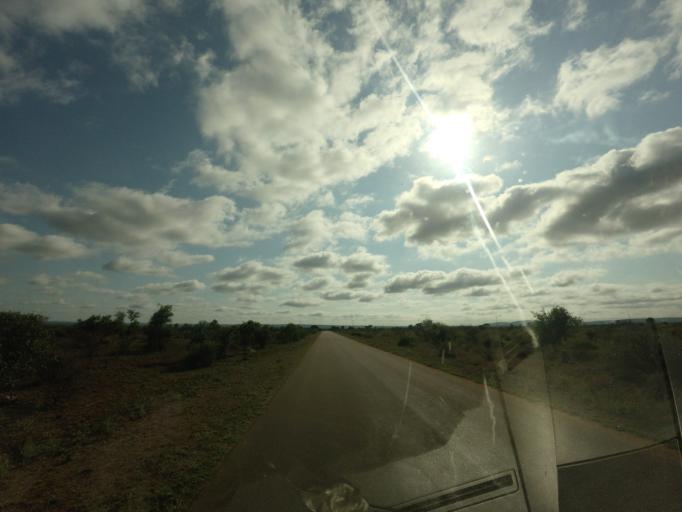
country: ZA
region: Mpumalanga
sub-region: Ehlanzeni District
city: Komatipoort
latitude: -25.1783
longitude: 31.9074
